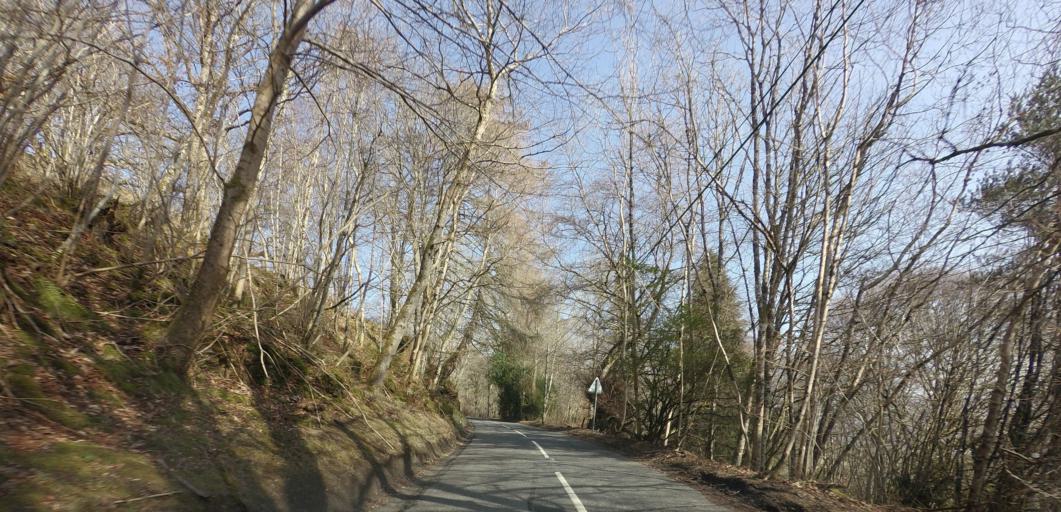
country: GB
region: Scotland
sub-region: Stirling
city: Callander
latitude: 56.4874
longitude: -4.2806
